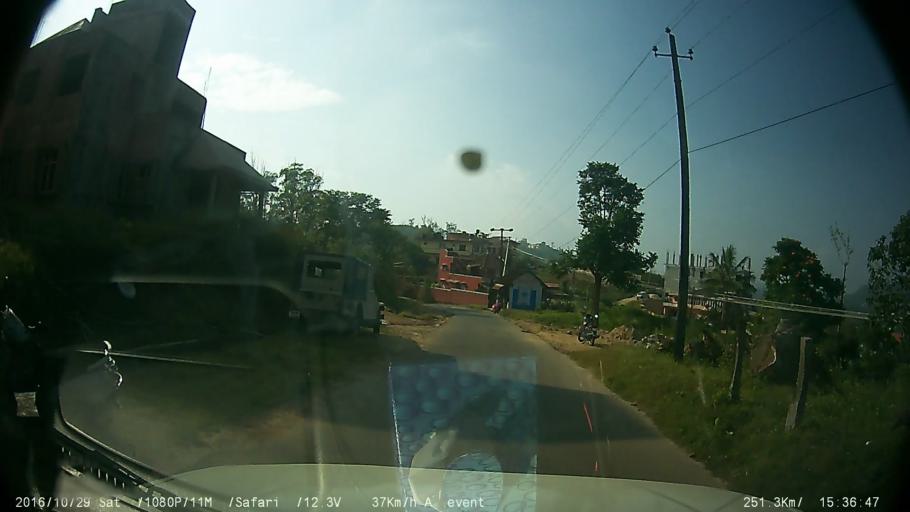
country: IN
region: Karnataka
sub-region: Kodagu
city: Madikeri
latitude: 12.4172
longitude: 75.7332
